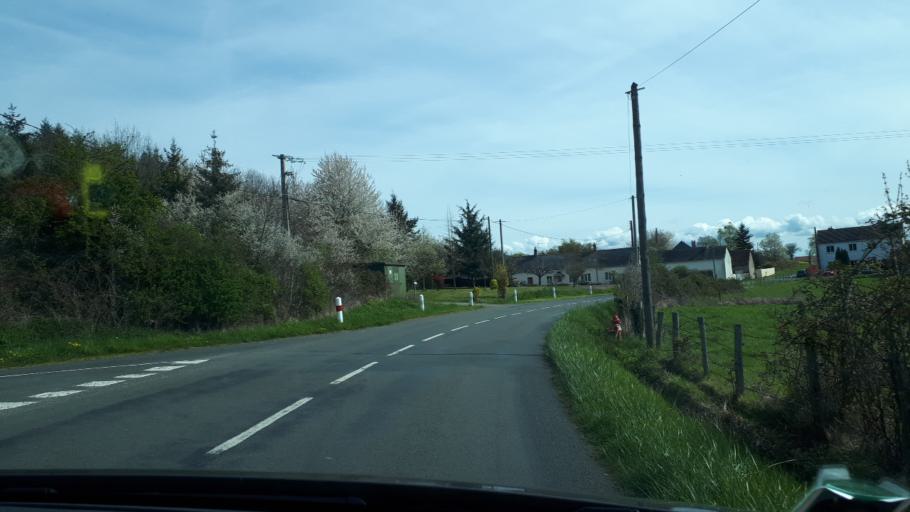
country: FR
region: Pays de la Loire
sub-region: Departement de la Sarthe
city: Yvre-le-Polin
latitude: 47.8228
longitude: 0.1638
